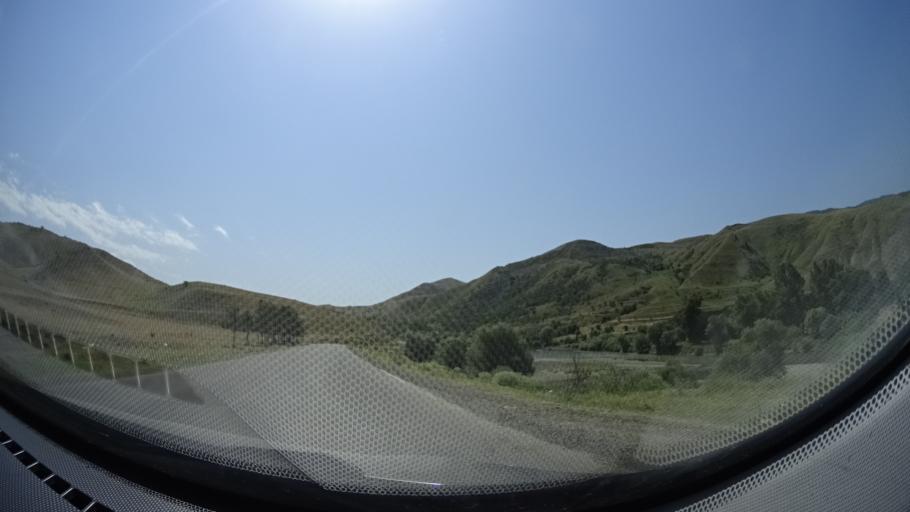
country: GE
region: Samtskhe-Javakheti
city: Aspindza
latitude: 41.5973
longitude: 43.1954
